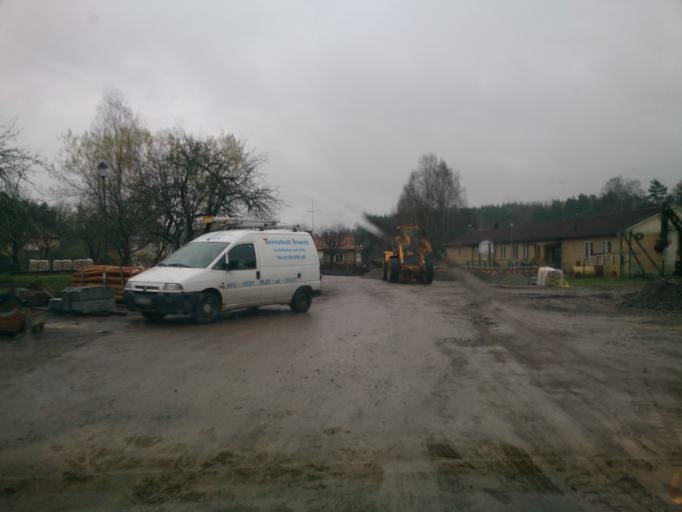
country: SE
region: OEstergoetland
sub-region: Atvidabergs Kommun
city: Atvidaberg
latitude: 58.2076
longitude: 16.0070
